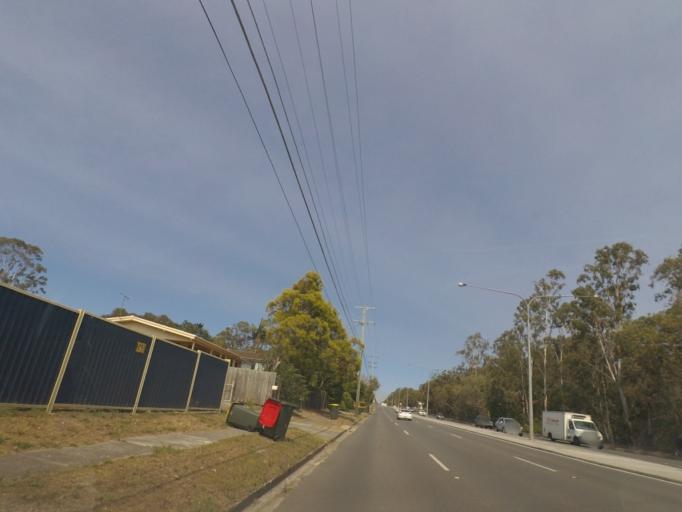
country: AU
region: Queensland
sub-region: Brisbane
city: Coopers Plains
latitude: -27.5579
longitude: 153.0453
